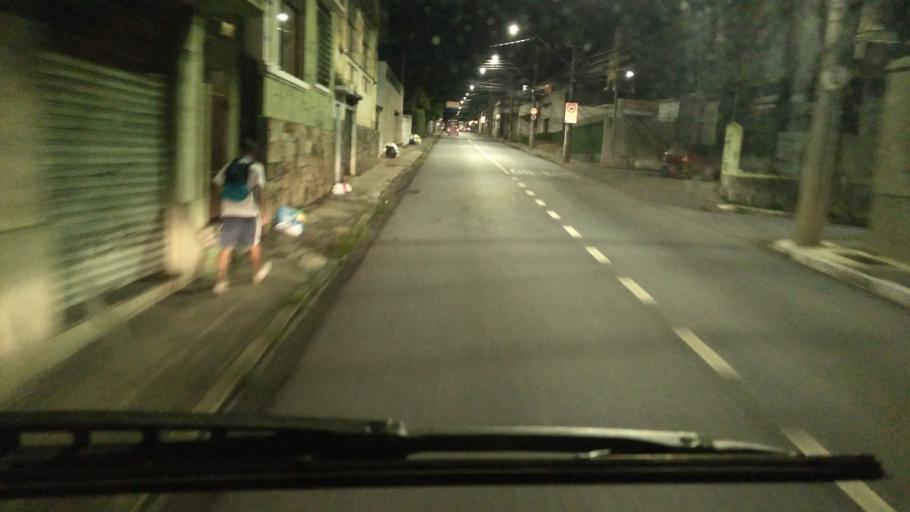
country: BR
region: Minas Gerais
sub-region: Belo Horizonte
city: Belo Horizonte
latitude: -19.9136
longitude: -43.9585
